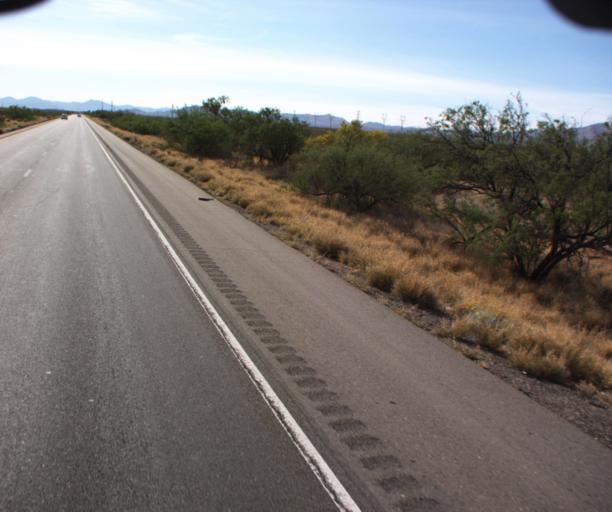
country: US
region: Arizona
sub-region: Pima County
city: Vail
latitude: 32.0420
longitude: -110.7431
